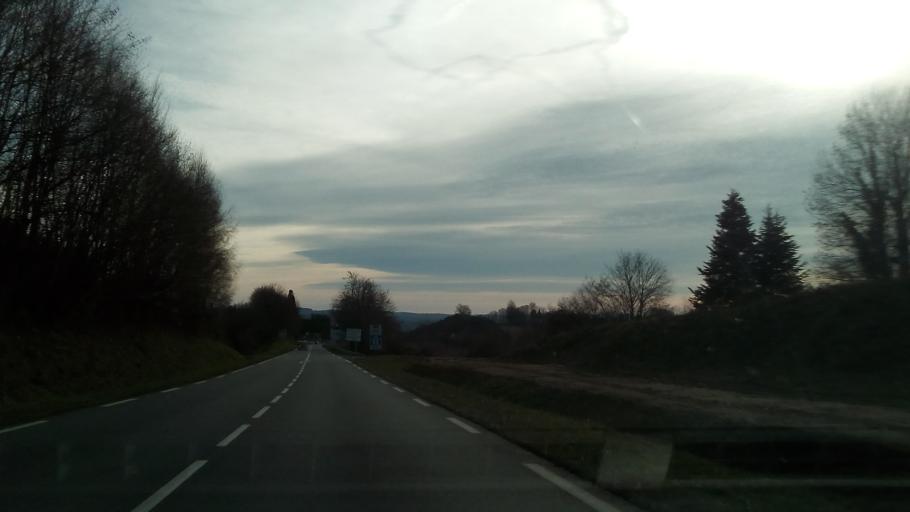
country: FR
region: Limousin
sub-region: Departement de la Correze
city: Naves
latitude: 45.3303
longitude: 1.7641
